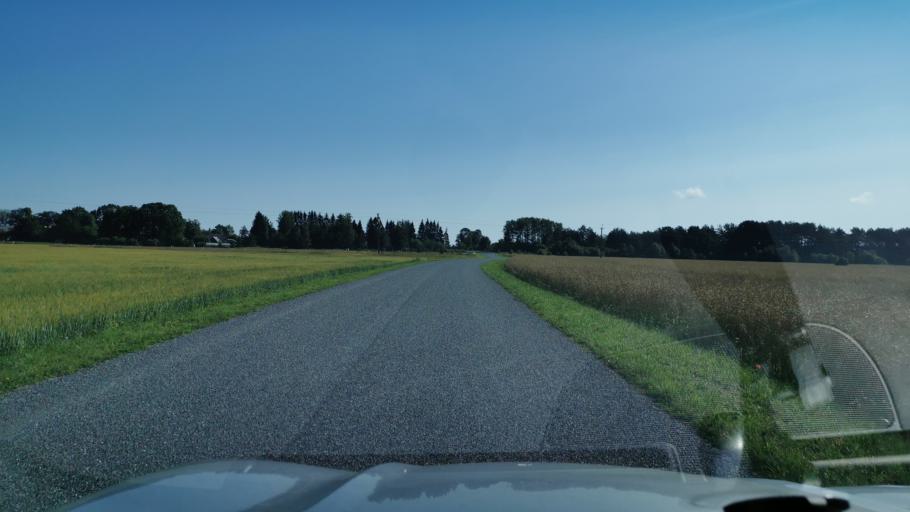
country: EE
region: Harju
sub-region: Paldiski linn
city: Paldiski
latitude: 59.2149
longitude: 24.0402
